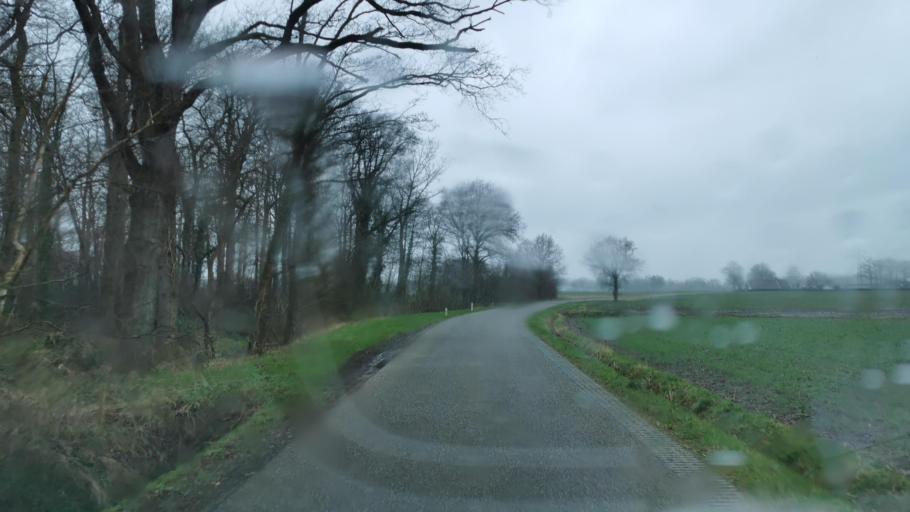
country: NL
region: Overijssel
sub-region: Gemeente Hengelo
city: Hengelo
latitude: 52.2993
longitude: 6.8555
